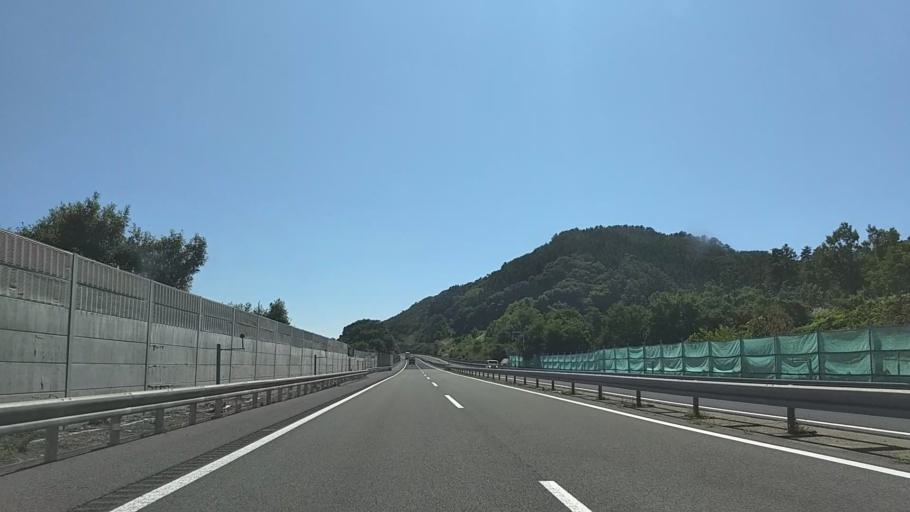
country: JP
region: Nagano
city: Nakano
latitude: 36.7699
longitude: 138.3177
